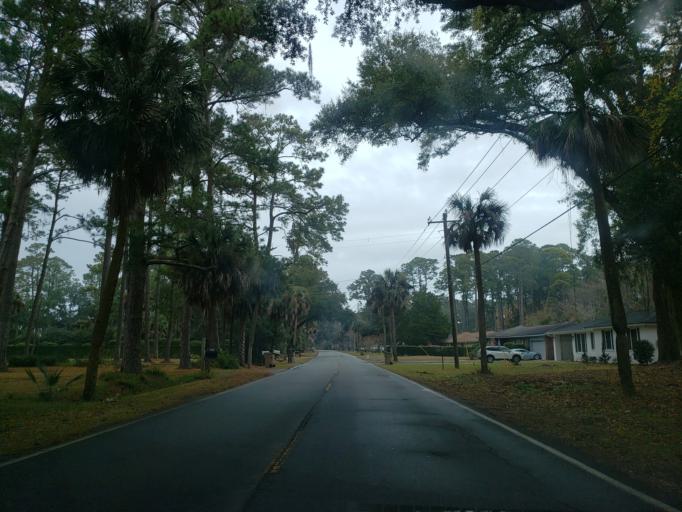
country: US
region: Georgia
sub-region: Chatham County
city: Wilmington Island
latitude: 31.9872
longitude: -80.9948
